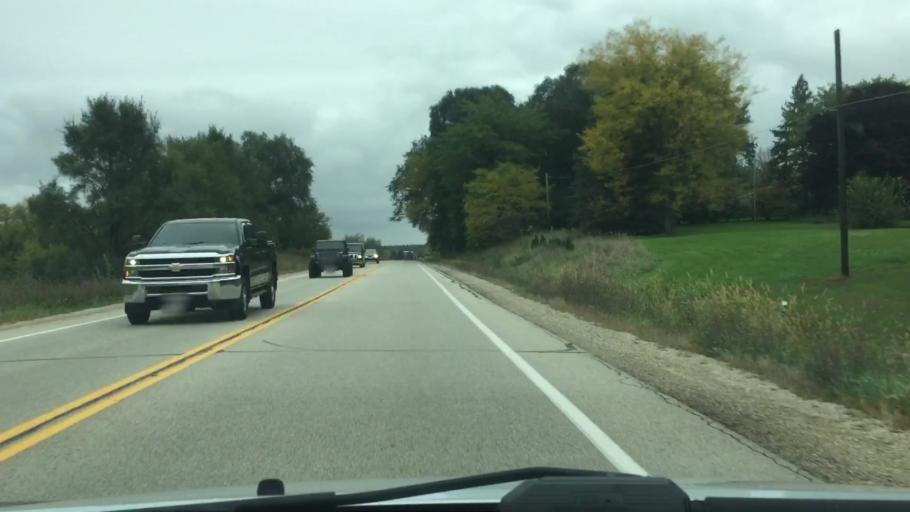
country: US
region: Wisconsin
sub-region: Walworth County
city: Elkhorn
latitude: 42.7399
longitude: -88.5514
